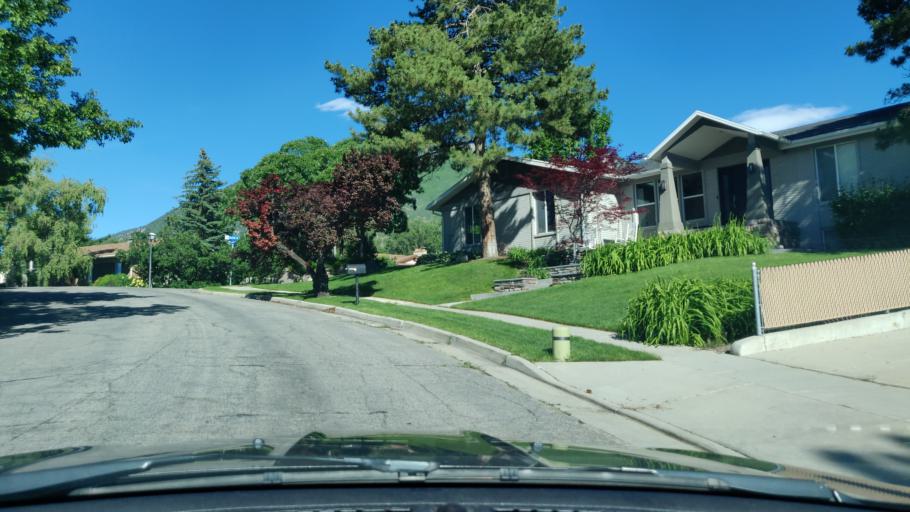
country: US
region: Utah
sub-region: Salt Lake County
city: Cottonwood Heights
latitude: 40.6132
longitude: -111.8091
